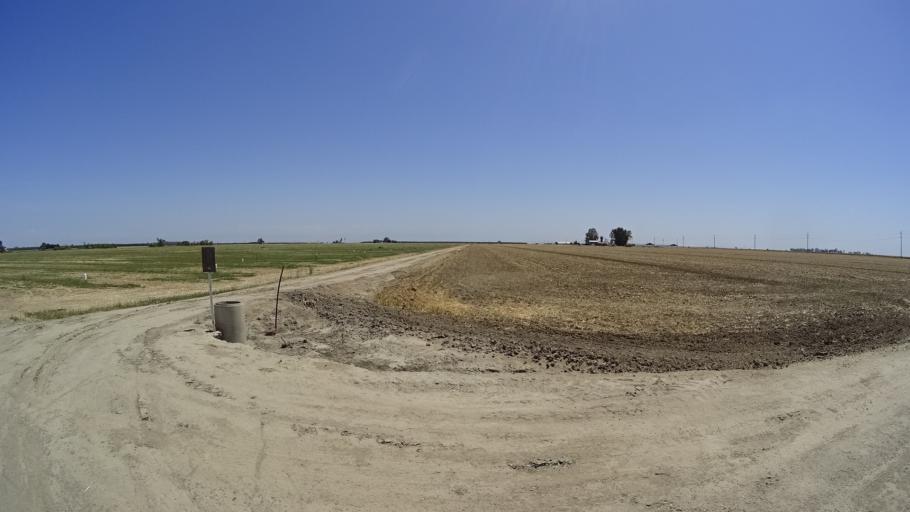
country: US
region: California
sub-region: Kings County
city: Armona
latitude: 36.2278
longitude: -119.7266
